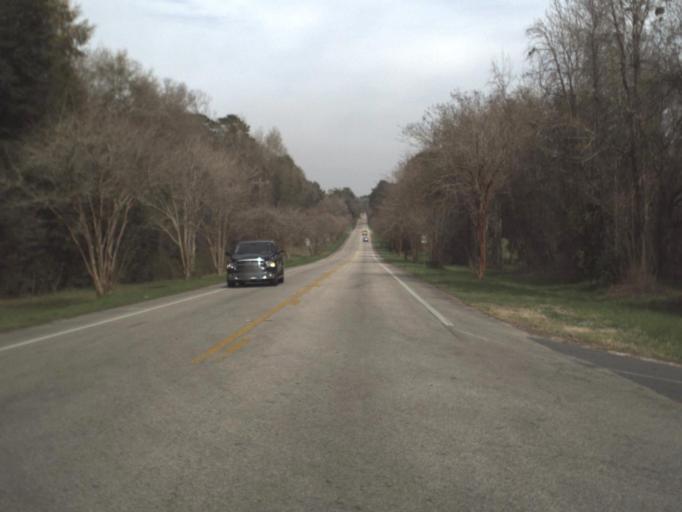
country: US
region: Florida
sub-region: Jefferson County
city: Monticello
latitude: 30.5415
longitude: -83.9096
